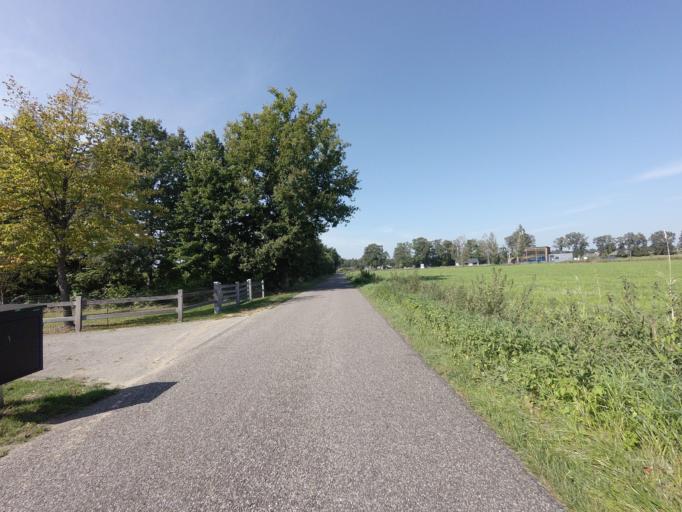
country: NL
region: Overijssel
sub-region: Gemeente Haaksbergen
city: Haaksbergen
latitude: 52.2125
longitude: 6.7552
